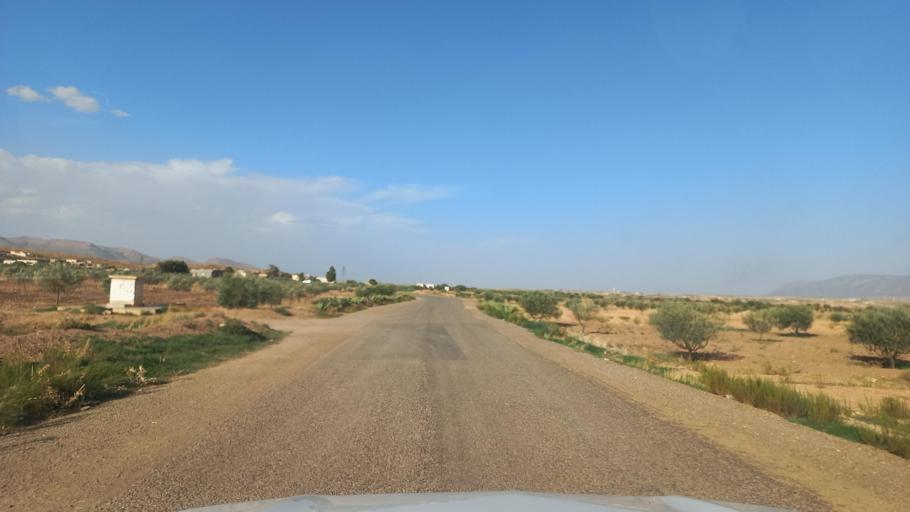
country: TN
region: Al Qasrayn
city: Sbiba
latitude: 35.3714
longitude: 9.0121
